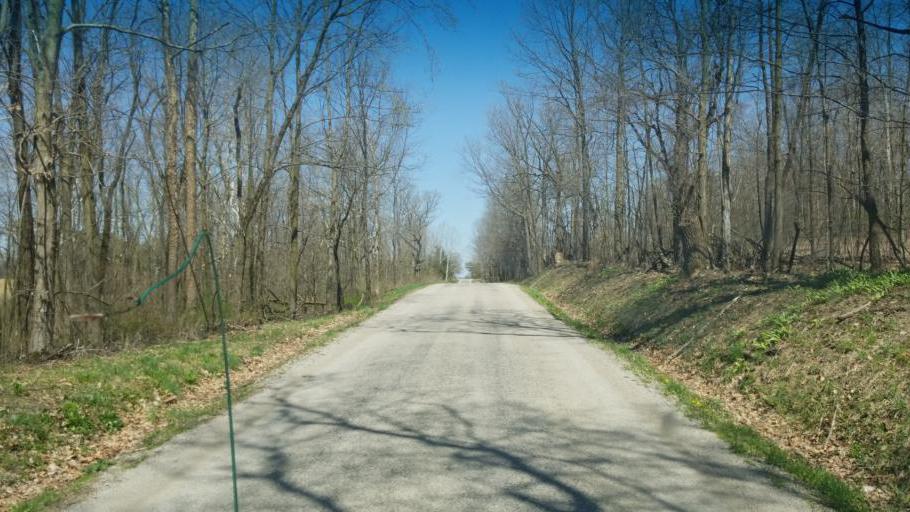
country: US
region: Ohio
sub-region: Huron County
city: New London
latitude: 41.0251
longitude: -82.4346
